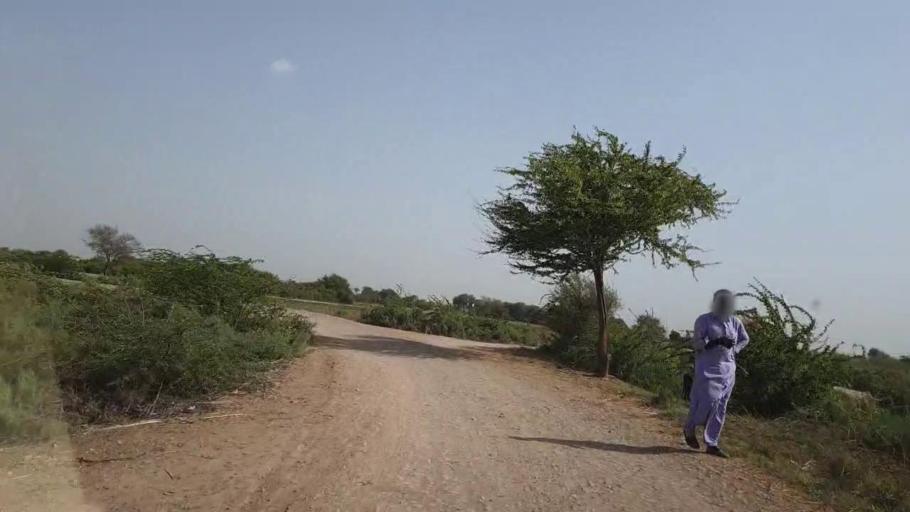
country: PK
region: Sindh
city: Rajo Khanani
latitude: 25.0493
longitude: 68.8428
